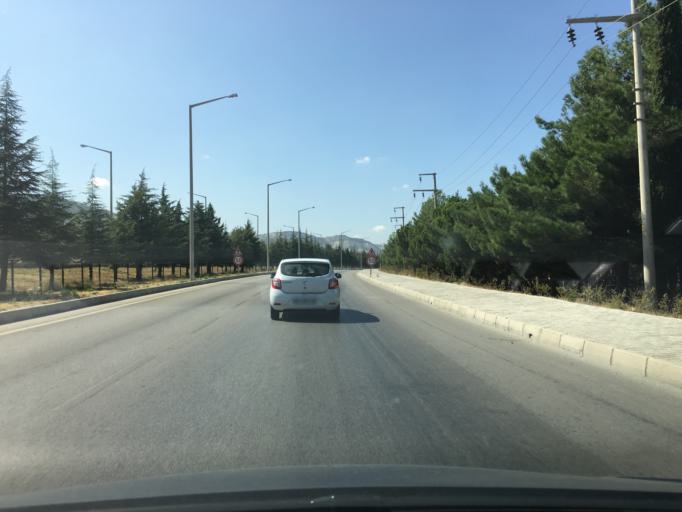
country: TR
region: Burdur
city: Burdur
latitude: 37.7347
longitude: 30.3100
